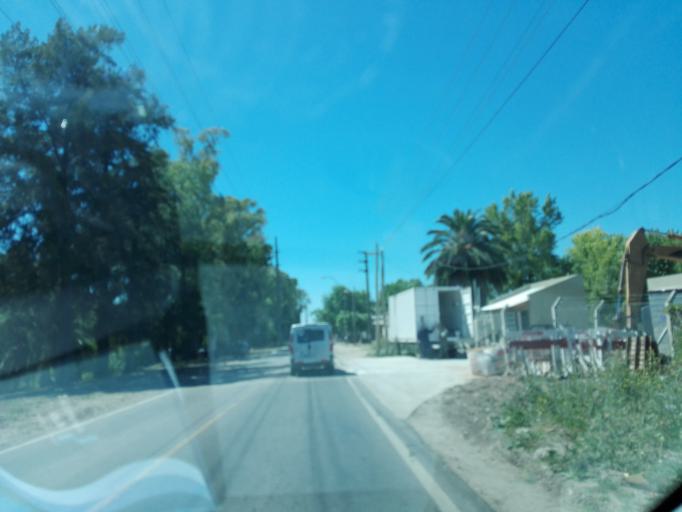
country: AR
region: Buenos Aires
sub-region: Partido de La Plata
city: La Plata
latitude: -34.8992
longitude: -57.9254
